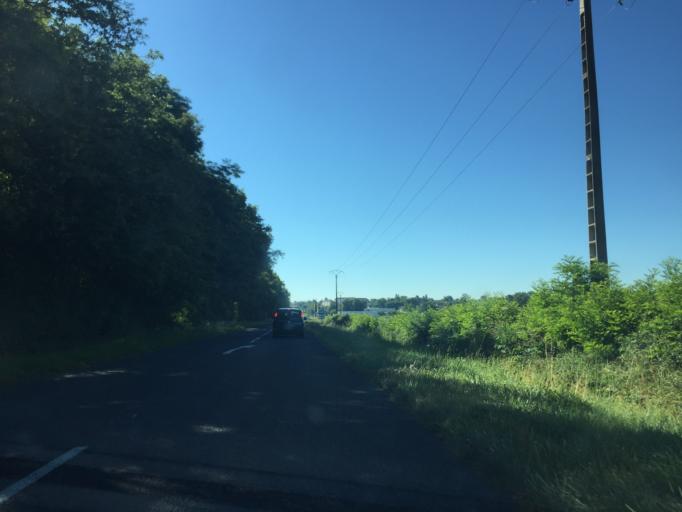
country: FR
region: Auvergne
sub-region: Departement de l'Allier
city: Dompierre-sur-Besbre
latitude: 46.5331
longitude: 3.6625
